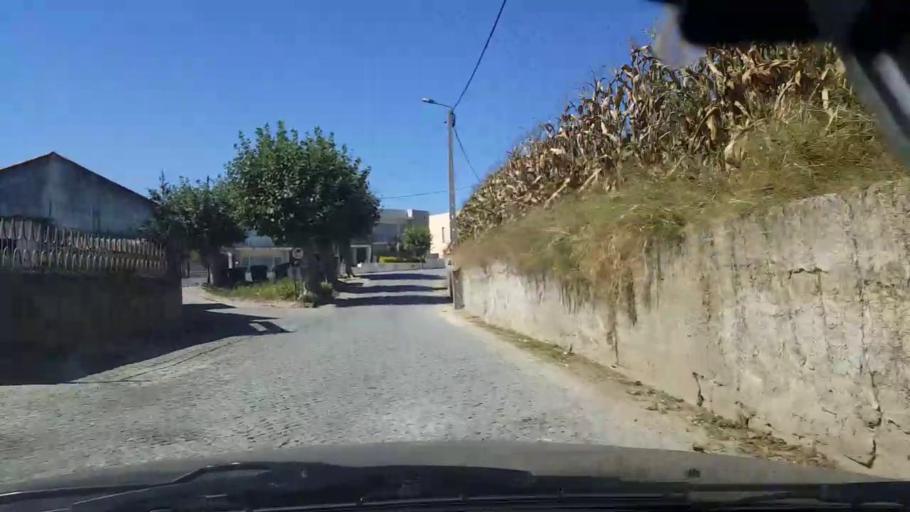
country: PT
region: Porto
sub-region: Vila do Conde
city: Arvore
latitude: 41.3367
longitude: -8.7162
